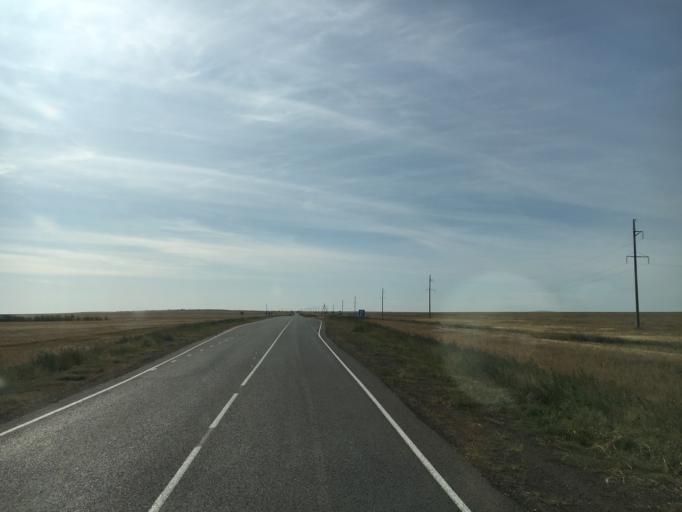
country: KZ
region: Batys Qazaqstan
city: Peremetnoe
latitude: 51.1172
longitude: 50.6281
